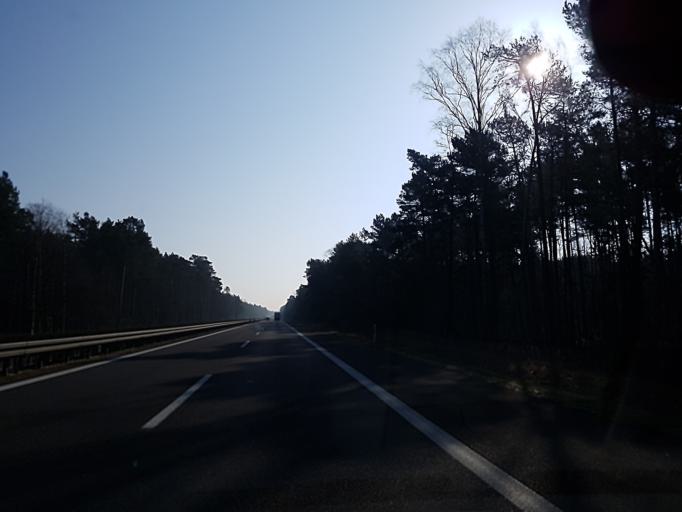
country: DE
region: Brandenburg
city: Forst
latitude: 51.7113
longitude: 14.5776
